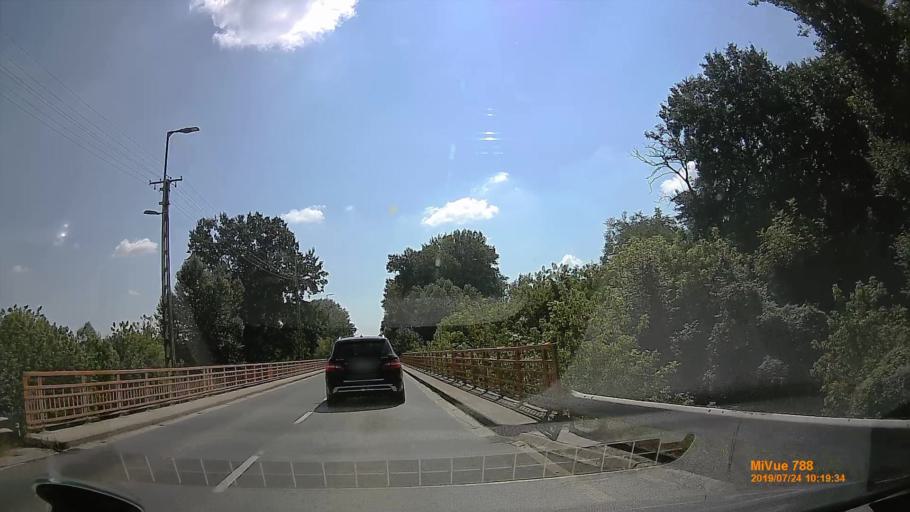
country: HU
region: Szabolcs-Szatmar-Bereg
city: Vasarosnameny
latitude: 48.1268
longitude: 22.3285
